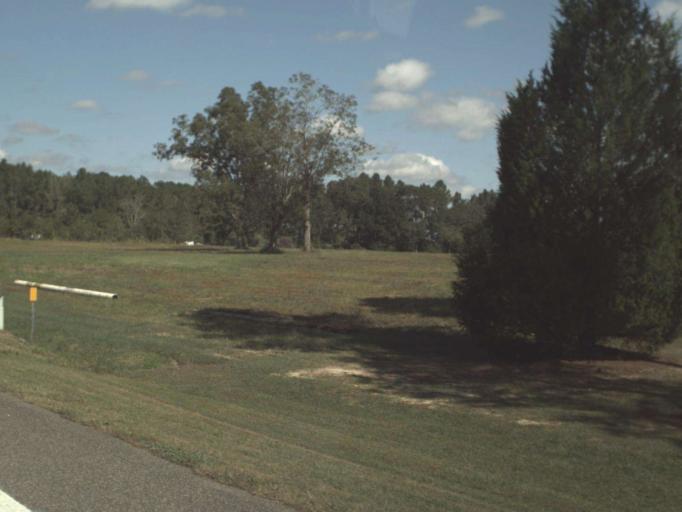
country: US
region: Florida
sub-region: Walton County
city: DeFuniak Springs
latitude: 30.8676
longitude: -86.1177
